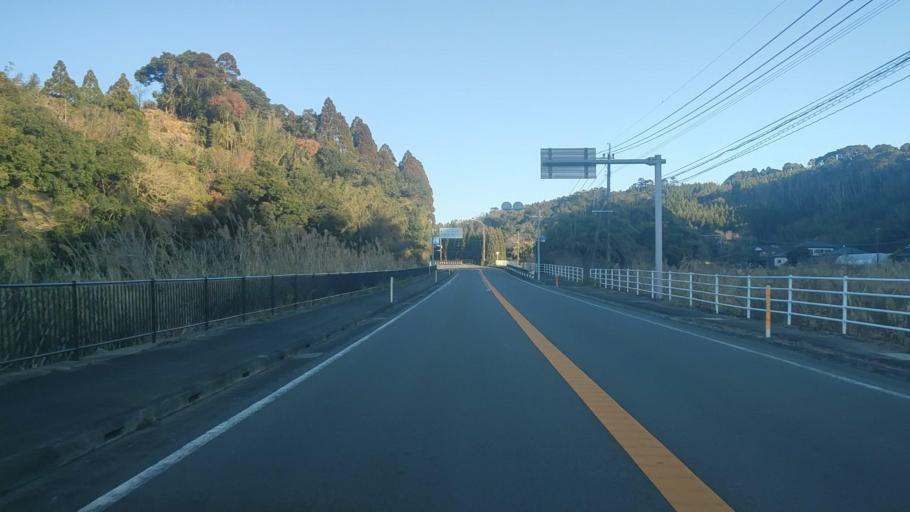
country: JP
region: Miyazaki
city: Takanabe
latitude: 32.1488
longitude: 131.5251
